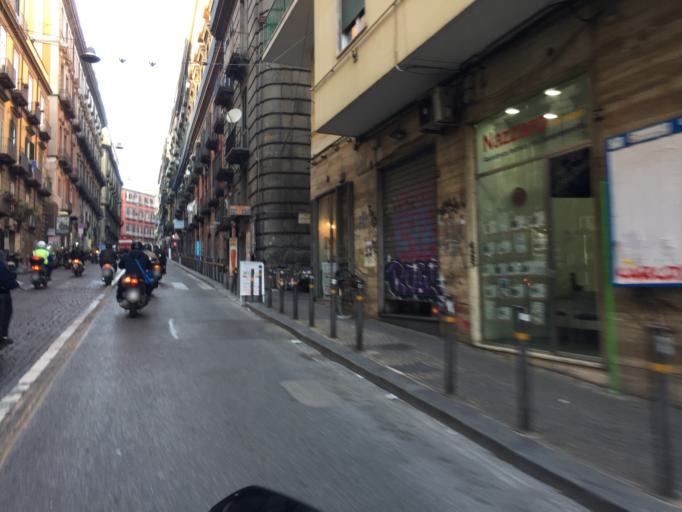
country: IT
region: Campania
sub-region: Provincia di Napoli
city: Napoli
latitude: 40.8456
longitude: 14.2509
